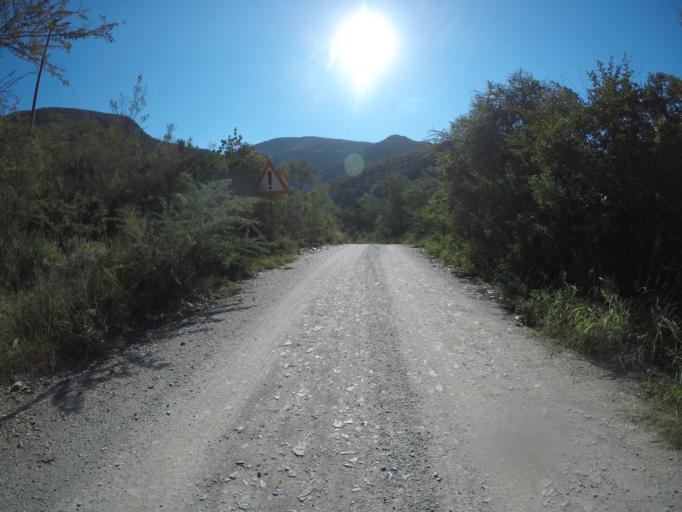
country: ZA
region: Eastern Cape
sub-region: Cacadu District Municipality
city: Kareedouw
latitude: -33.6622
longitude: 24.5405
